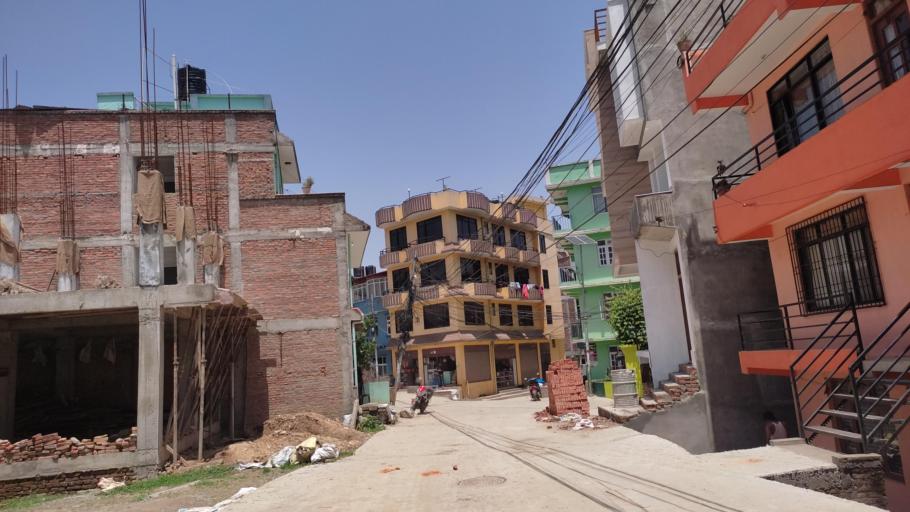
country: NP
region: Central Region
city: Kirtipur
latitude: 27.6750
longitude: 85.2735
